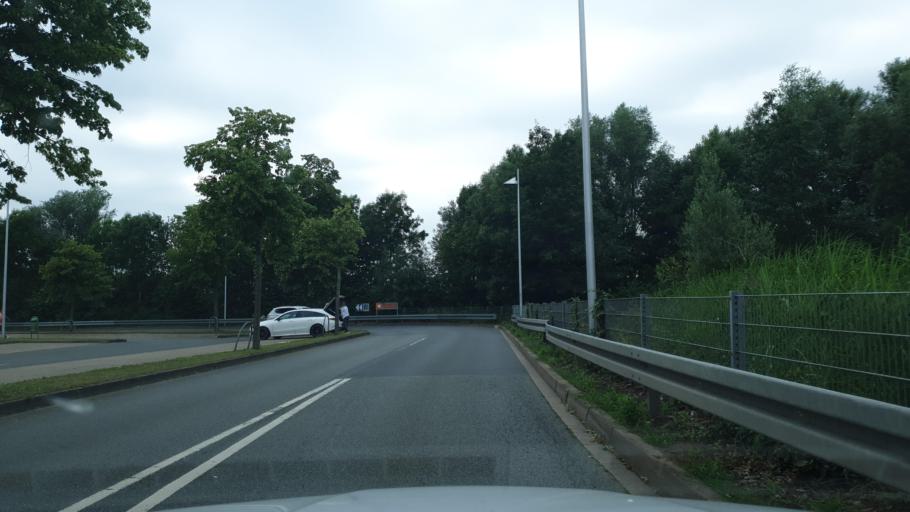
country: DE
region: North Rhine-Westphalia
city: Bad Oeynhausen
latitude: 52.2159
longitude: 8.8162
